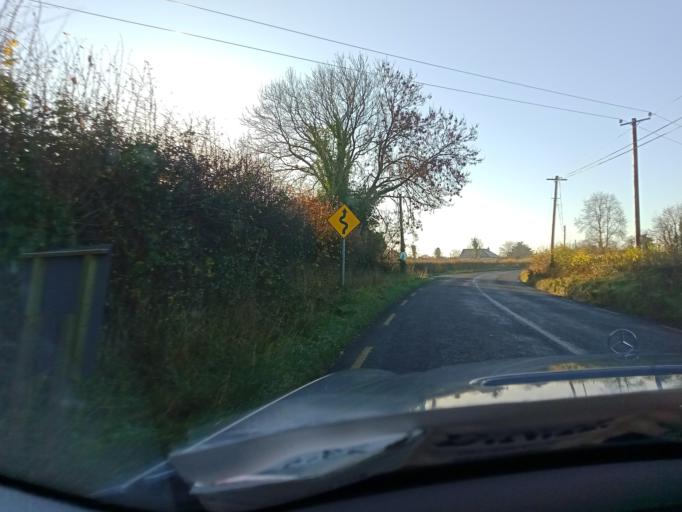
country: IE
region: Leinster
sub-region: Kilkenny
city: Callan
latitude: 52.5257
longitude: -7.3823
